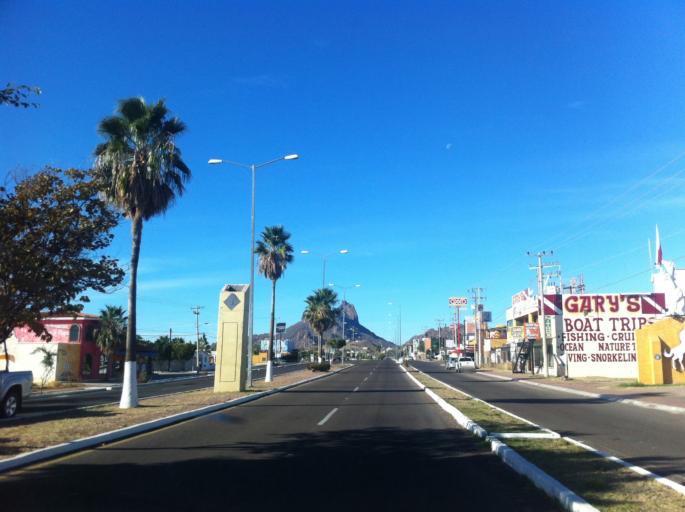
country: MX
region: Sonora
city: Heroica Guaymas
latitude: 27.9607
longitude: -111.0330
